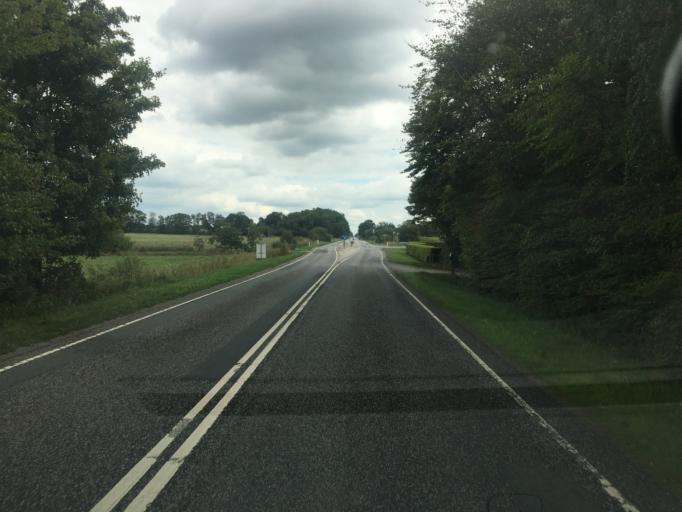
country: DK
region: South Denmark
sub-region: Tonder Kommune
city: Toftlund
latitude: 55.1222
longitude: 9.0730
